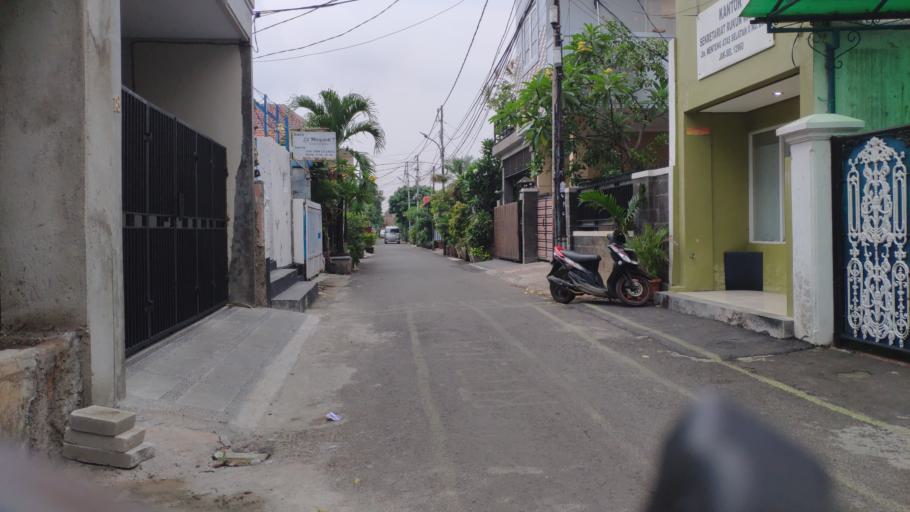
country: ID
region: Jakarta Raya
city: Jakarta
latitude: -6.2165
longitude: 106.8385
